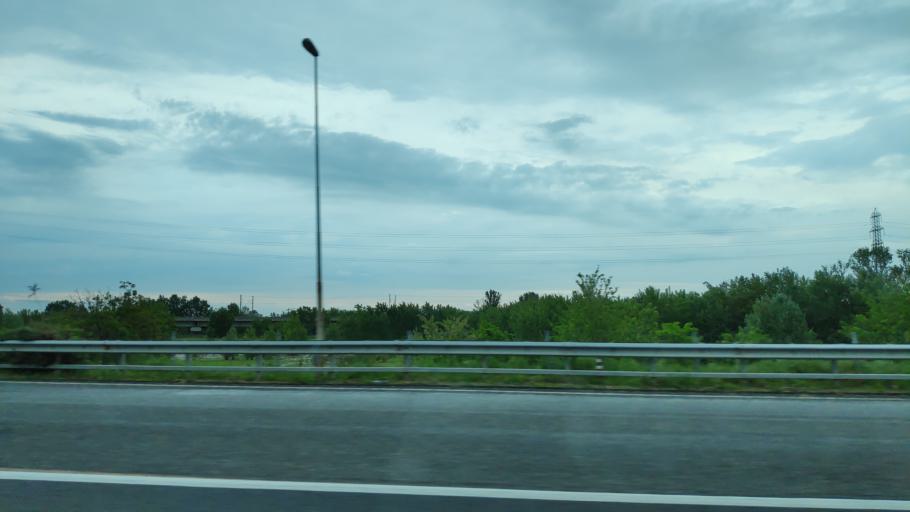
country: IT
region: Emilia-Romagna
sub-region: Provincia di Parma
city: Ponte Taro
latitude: 44.8641
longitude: 10.2381
